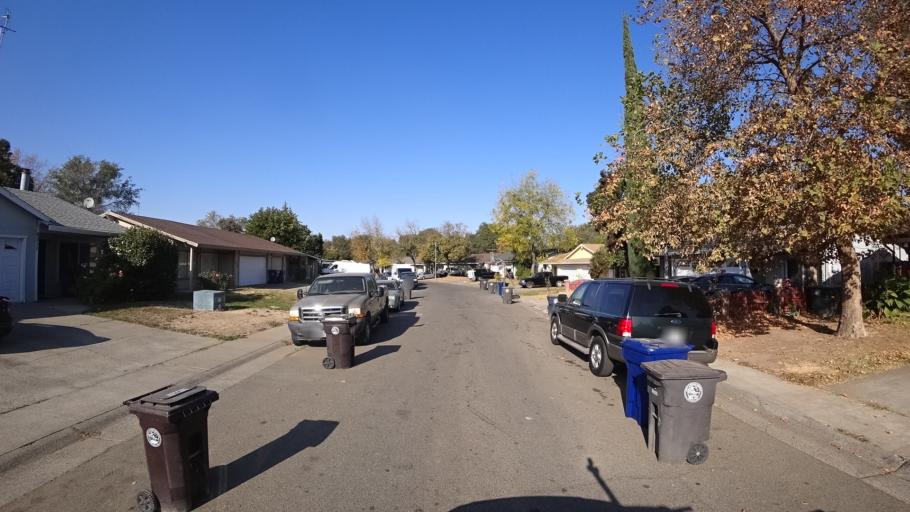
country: US
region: California
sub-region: Sacramento County
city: Citrus Heights
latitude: 38.6829
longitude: -121.2768
